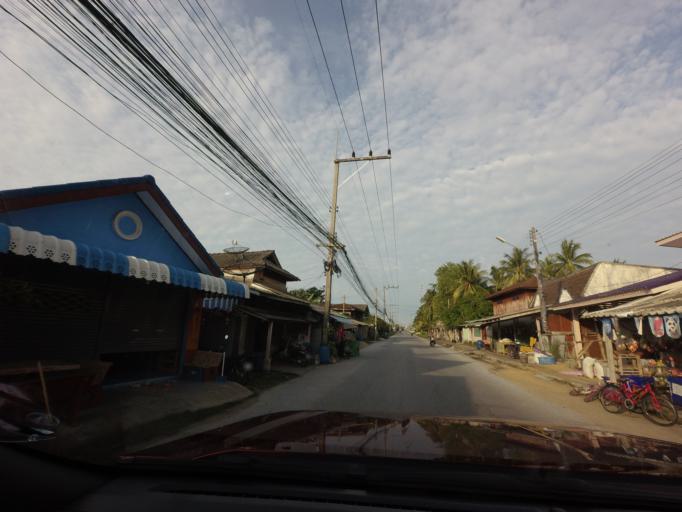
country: TH
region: Pattani
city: Yaring
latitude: 6.8694
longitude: 101.3438
